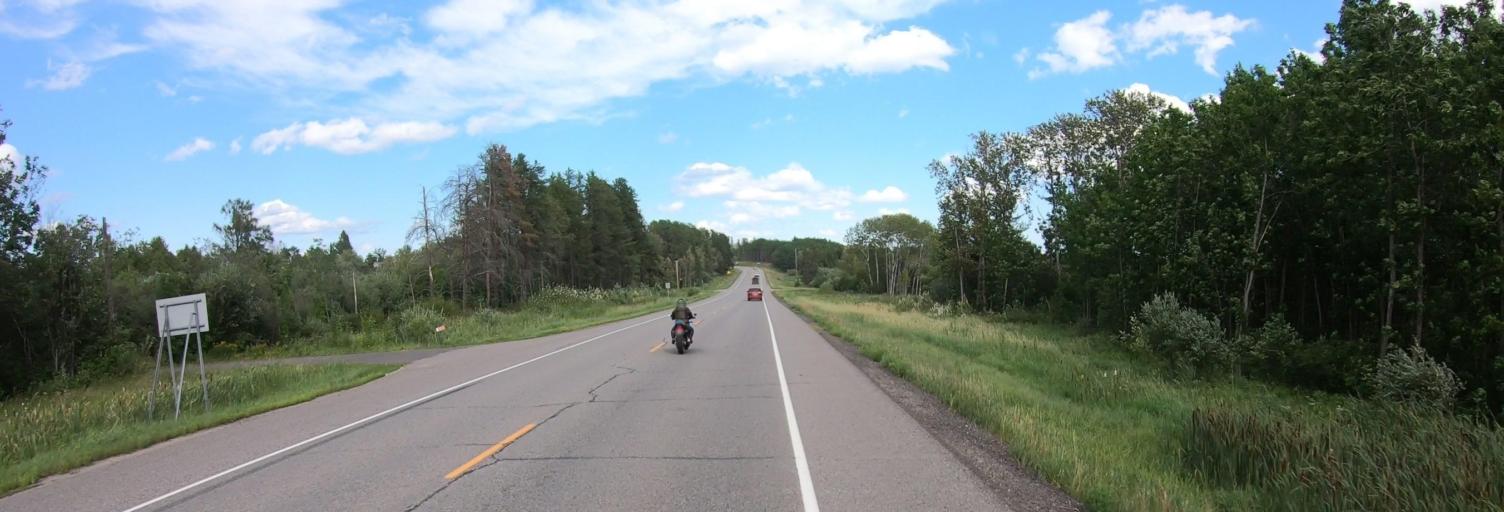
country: US
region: Minnesota
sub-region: Saint Louis County
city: Aurora
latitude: 47.8129
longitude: -92.2378
